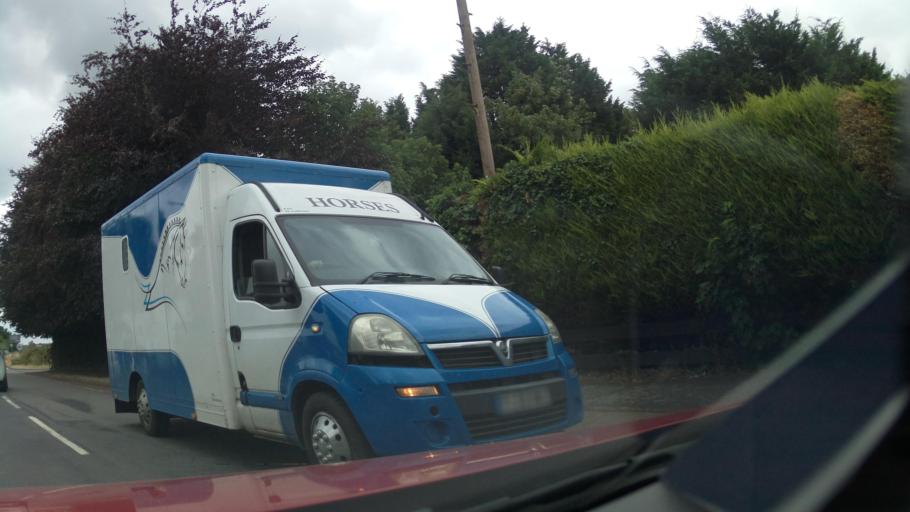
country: GB
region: England
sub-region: Derbyshire
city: Long Eaton
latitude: 52.9018
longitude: -1.3168
